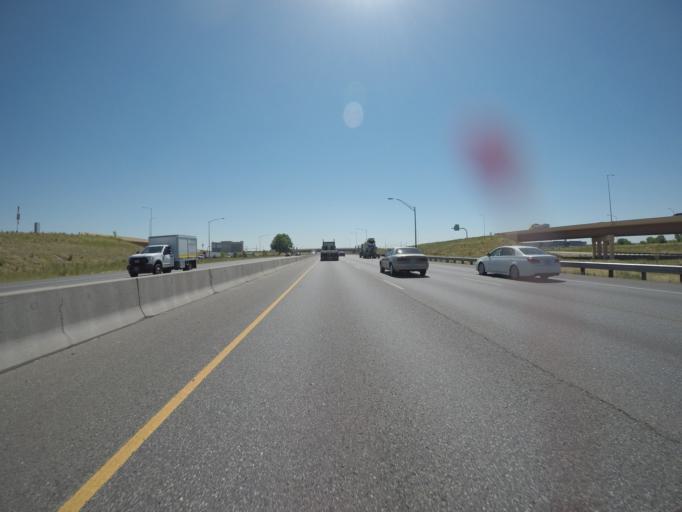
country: US
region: Colorado
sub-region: Adams County
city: Commerce City
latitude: 39.7776
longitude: -104.8884
